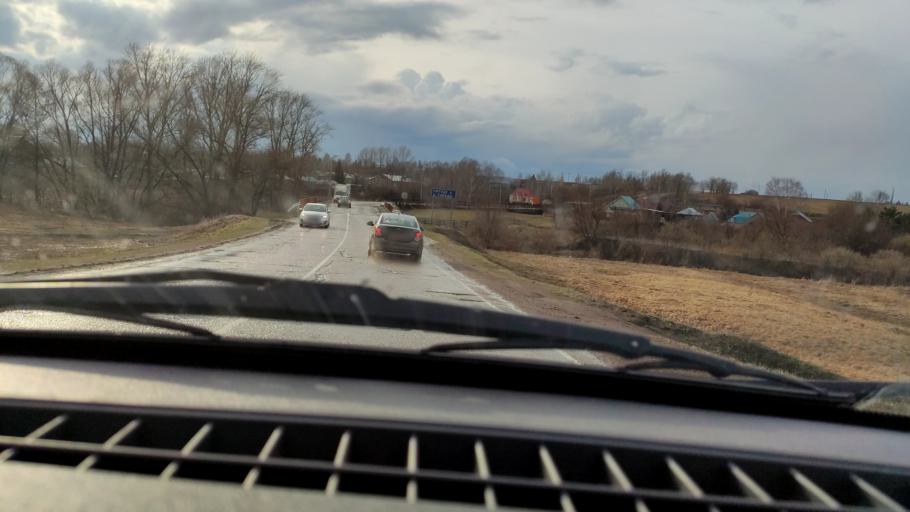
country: RU
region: Bashkortostan
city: Kushnarenkovo
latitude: 55.0918
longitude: 55.0600
